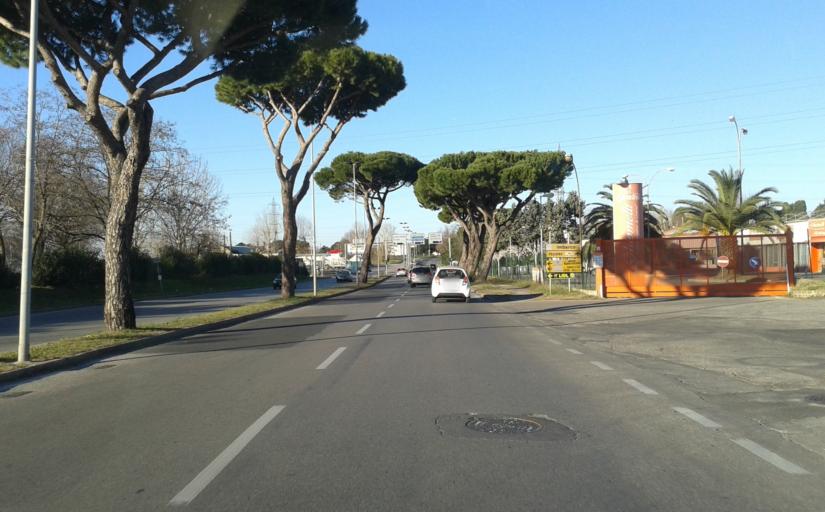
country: IT
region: Tuscany
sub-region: Provincia di Livorno
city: Livorno
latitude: 43.5664
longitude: 10.3243
